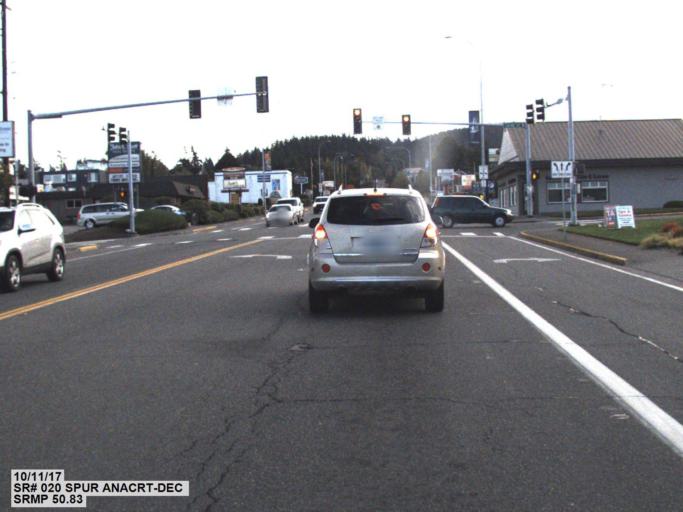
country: US
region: Washington
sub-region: Jefferson County
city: Port Hadlock-Irondale
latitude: 48.0041
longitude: -122.8361
